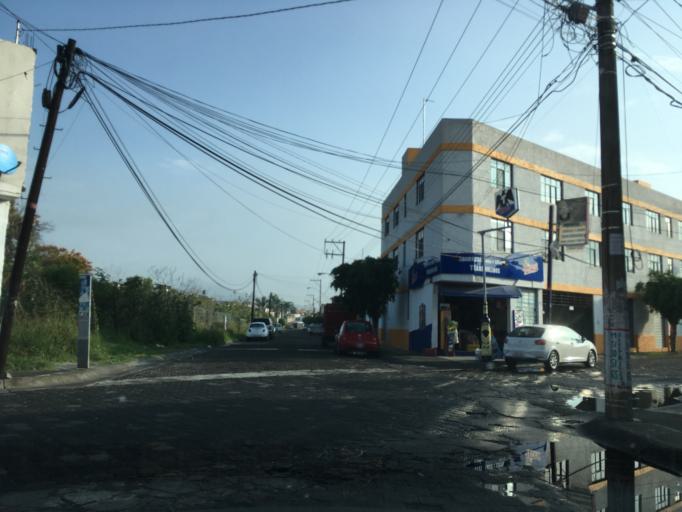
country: MX
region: Michoacan
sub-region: Morelia
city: Morelos
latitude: 19.6819
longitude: -101.2240
